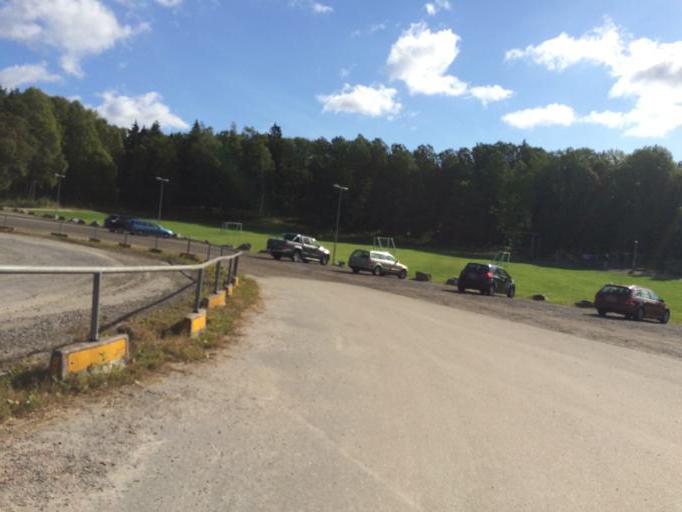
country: SE
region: Stockholm
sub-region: Haninge Kommun
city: Handen
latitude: 59.2230
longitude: 18.1030
